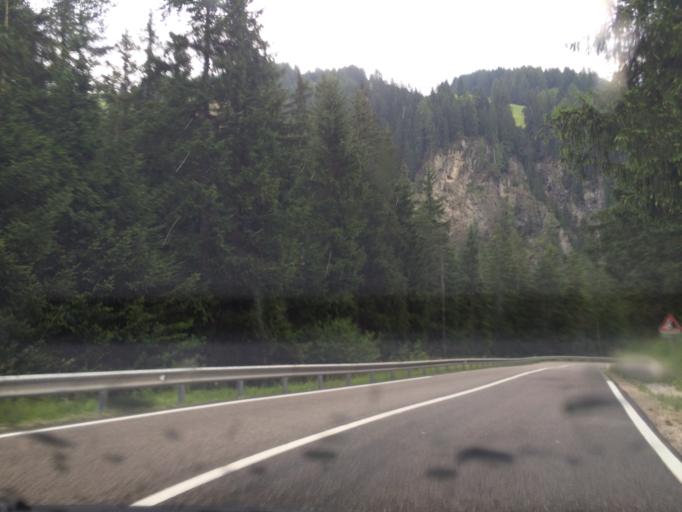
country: IT
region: Trentino-Alto Adige
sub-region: Bolzano
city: Badia
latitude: 46.6192
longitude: 11.8924
